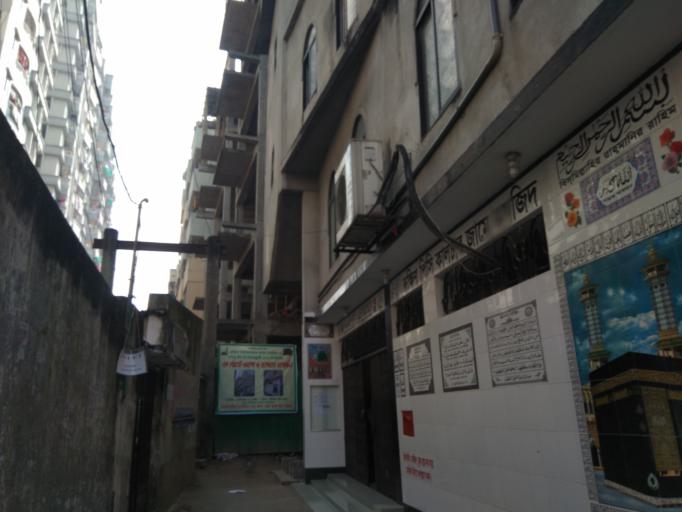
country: BD
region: Dhaka
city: Azimpur
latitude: 23.7653
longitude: 90.3565
